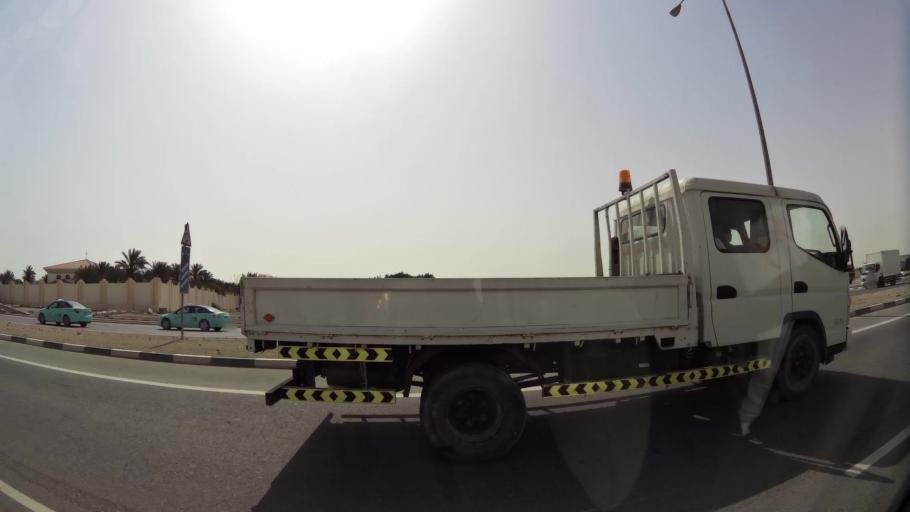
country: QA
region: Baladiyat ad Dawhah
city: Doha
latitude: 25.2354
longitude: 51.5202
